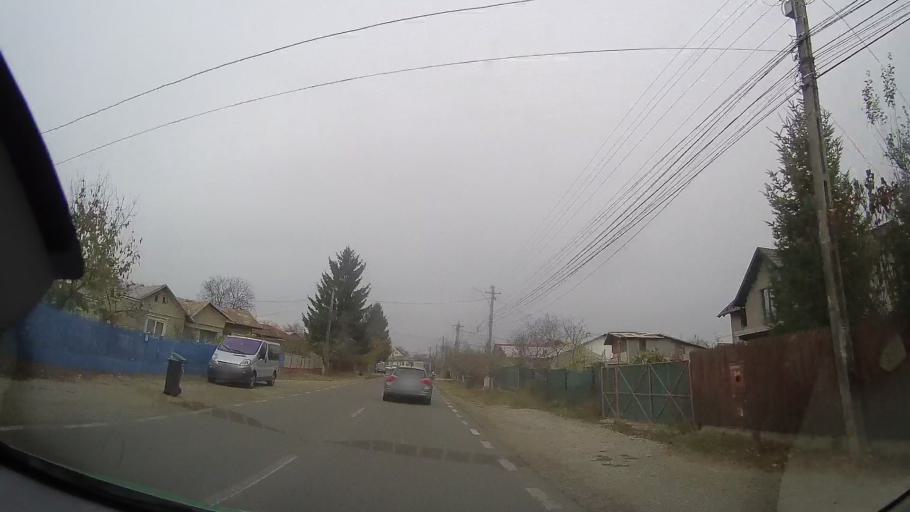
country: RO
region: Prahova
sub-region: Oras Baicoi
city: Liliesti
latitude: 45.0295
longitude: 25.8869
